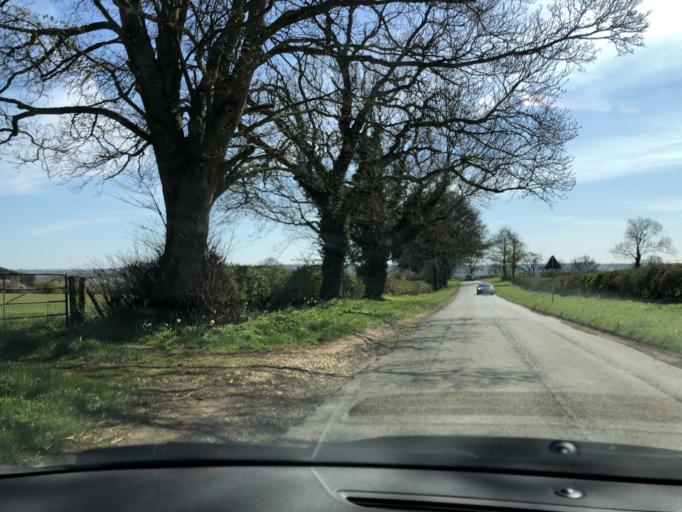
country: GB
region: England
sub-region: Oxfordshire
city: Hook Norton
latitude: 52.0105
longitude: -1.4405
